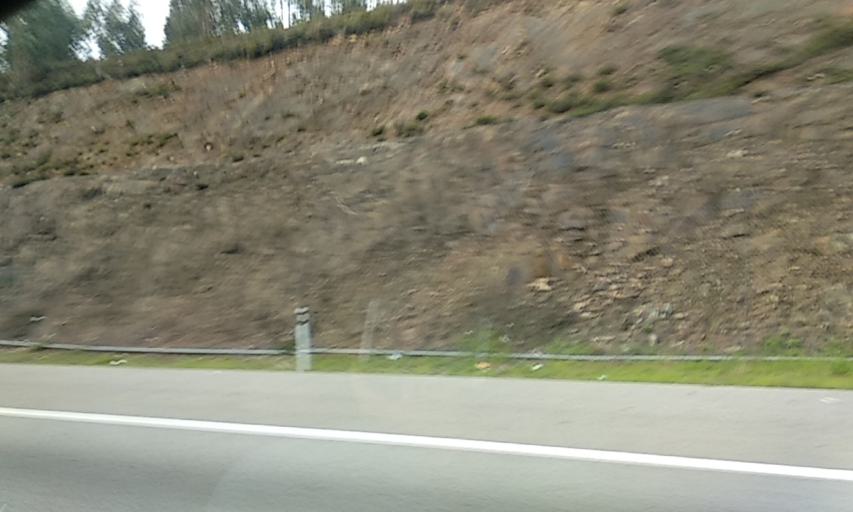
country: PT
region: Porto
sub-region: Trofa
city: Bougado
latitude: 41.3297
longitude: -8.5163
